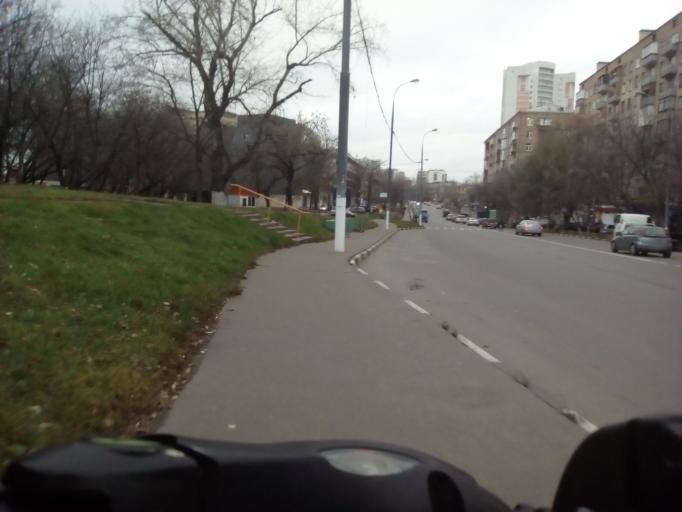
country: RU
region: Moscow
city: Lefortovo
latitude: 55.7631
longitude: 37.7184
